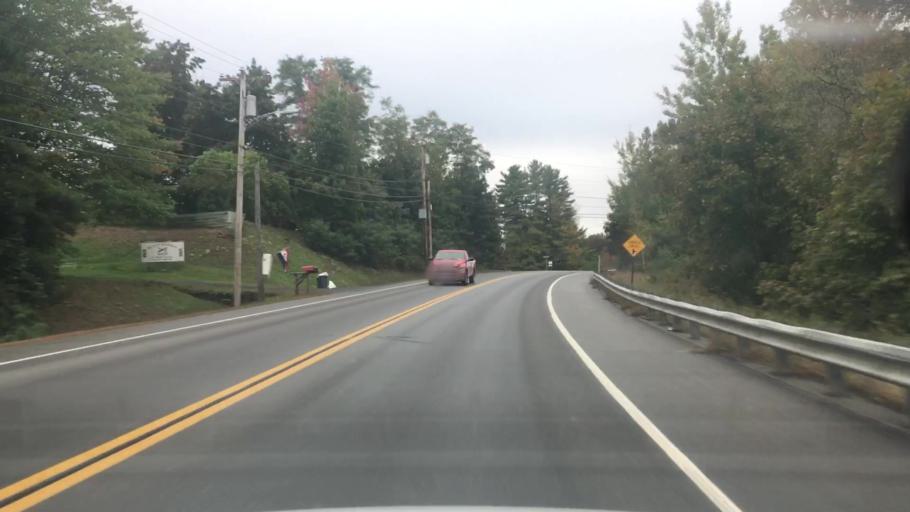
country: US
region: Maine
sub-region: Kennebec County
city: Augusta
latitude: 44.3799
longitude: -69.8014
